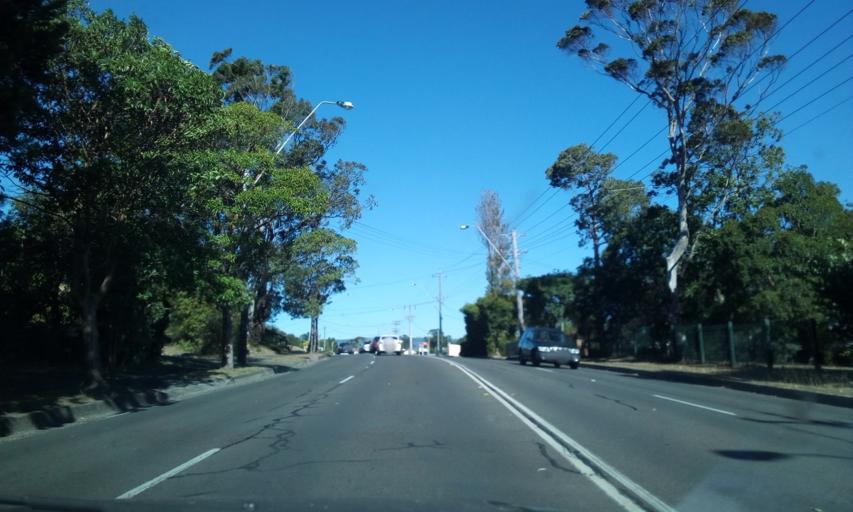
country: AU
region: New South Wales
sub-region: Wollongong
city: Dapto
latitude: -34.5039
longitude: 150.7879
